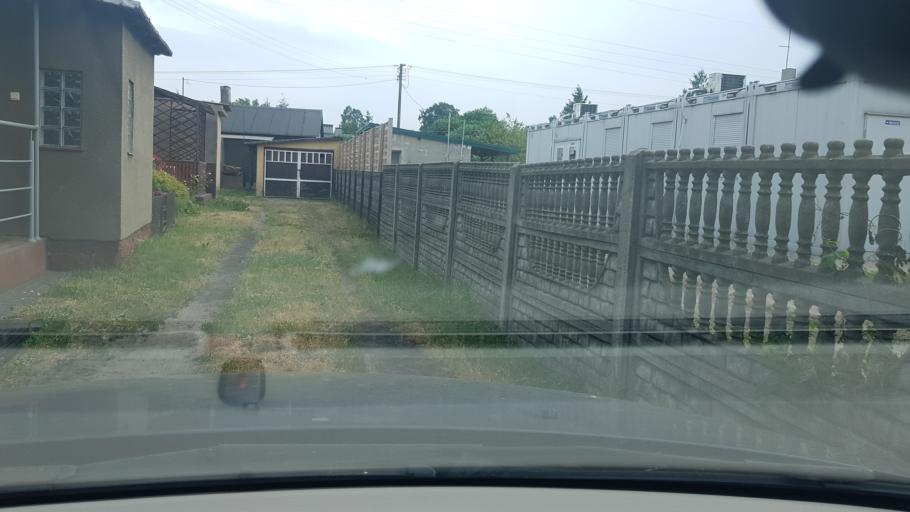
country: PL
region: Lodz Voivodeship
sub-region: Powiat tomaszowski
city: Tomaszow Mazowiecki
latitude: 51.5520
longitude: 20.0243
